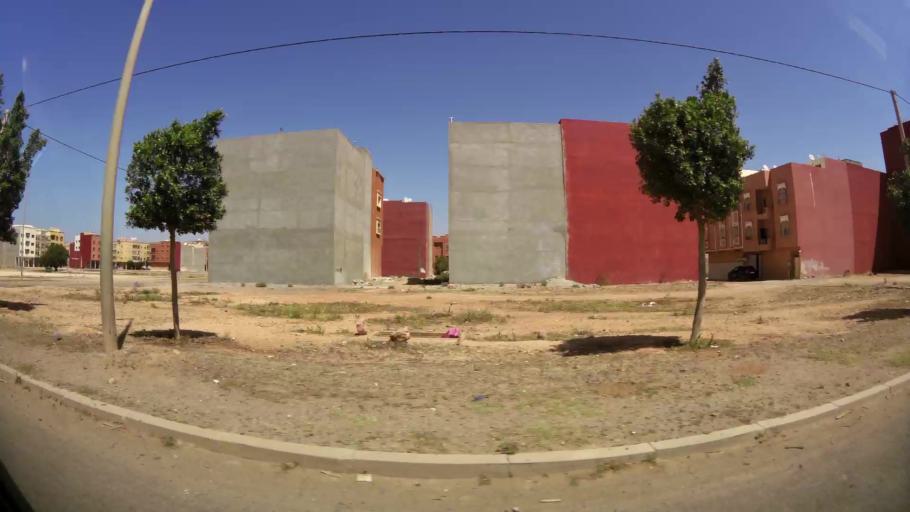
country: MA
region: Souss-Massa-Draa
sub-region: Inezgane-Ait Mellou
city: Inezgane
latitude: 30.3212
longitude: -9.4982
